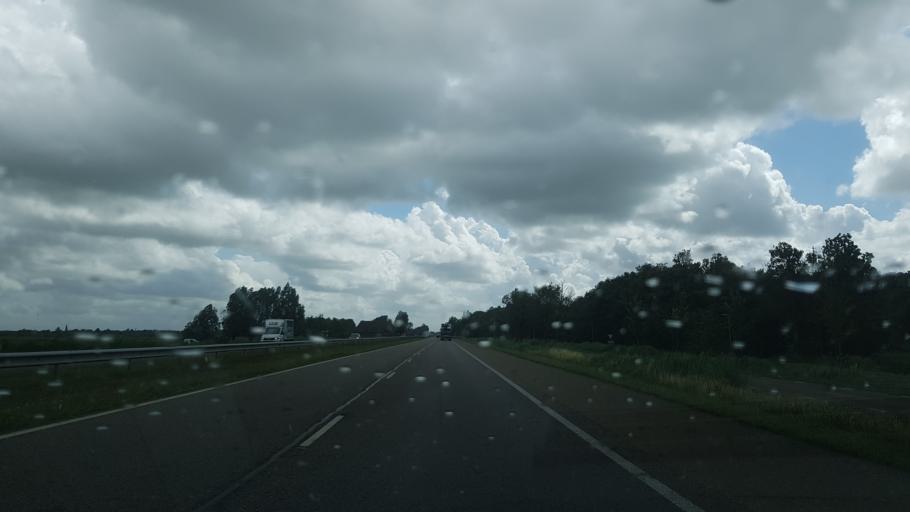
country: NL
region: Friesland
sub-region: Gemeente Tytsjerksteradiel
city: Tytsjerk
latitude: 53.2179
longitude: 5.8830
